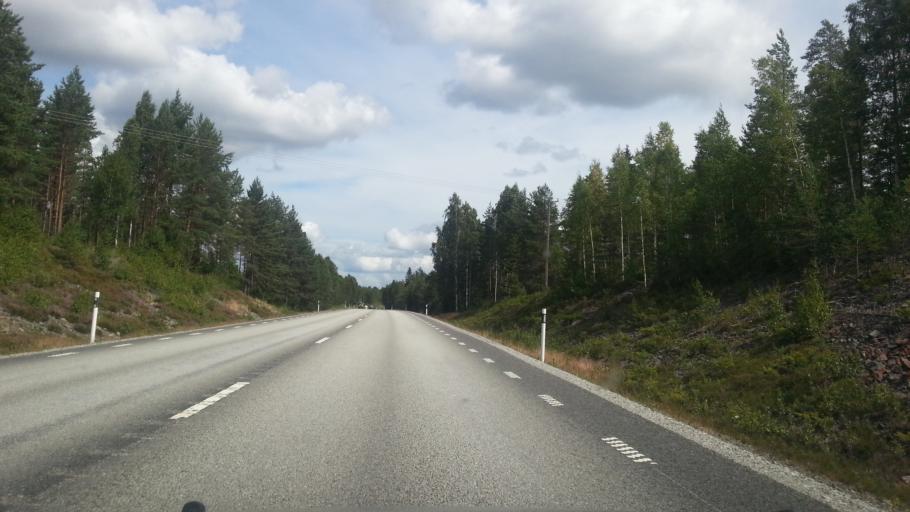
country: SE
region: Vaestmanland
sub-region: Skinnskattebergs Kommun
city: Skinnskatteberg
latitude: 59.7620
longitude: 15.4774
